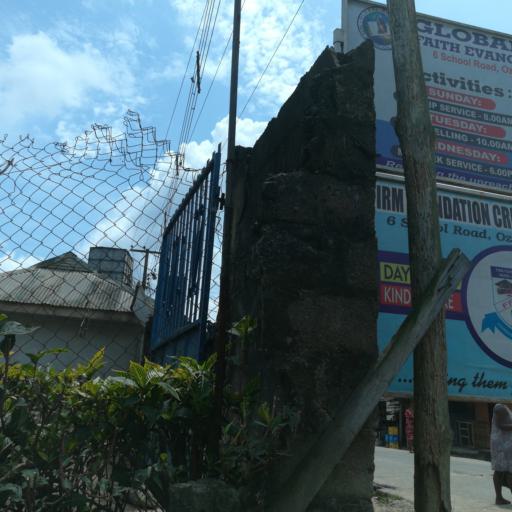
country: NG
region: Rivers
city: Port Harcourt
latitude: 4.7763
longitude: 7.0428
